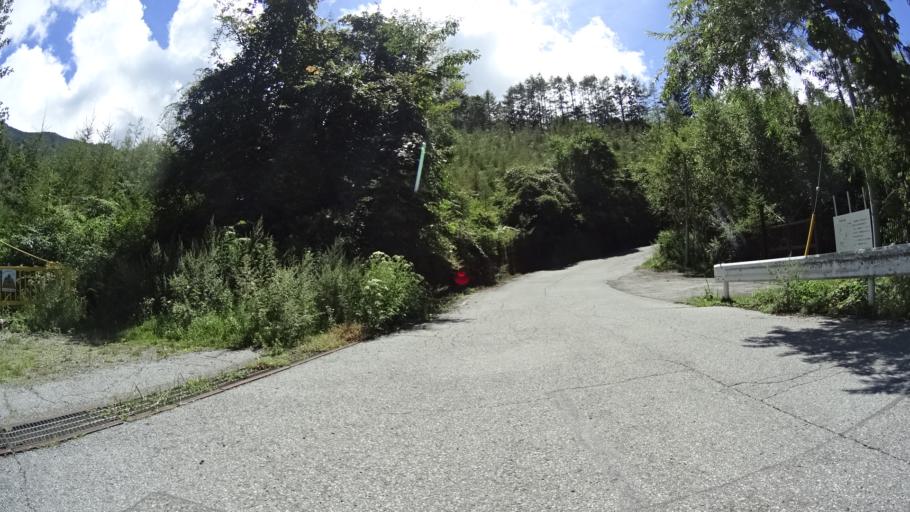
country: JP
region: Yamanashi
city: Enzan
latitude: 35.7235
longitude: 138.8419
